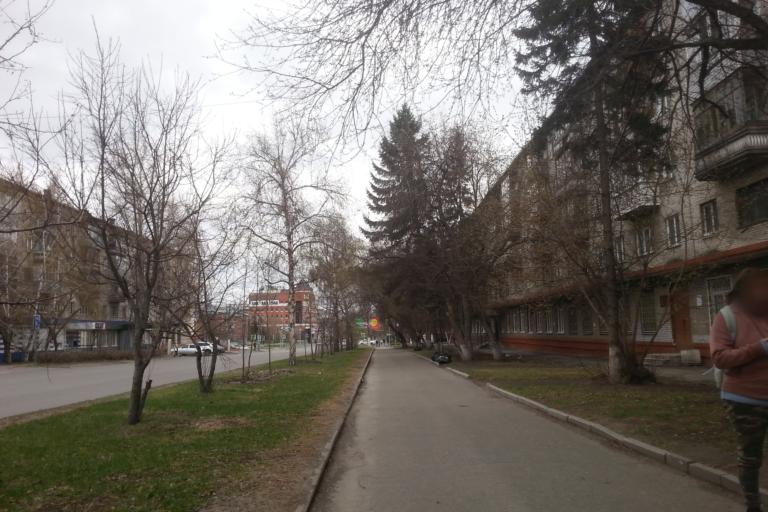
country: RU
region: Altai Krai
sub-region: Gorod Barnaulskiy
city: Barnaul
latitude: 53.3520
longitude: 83.7808
